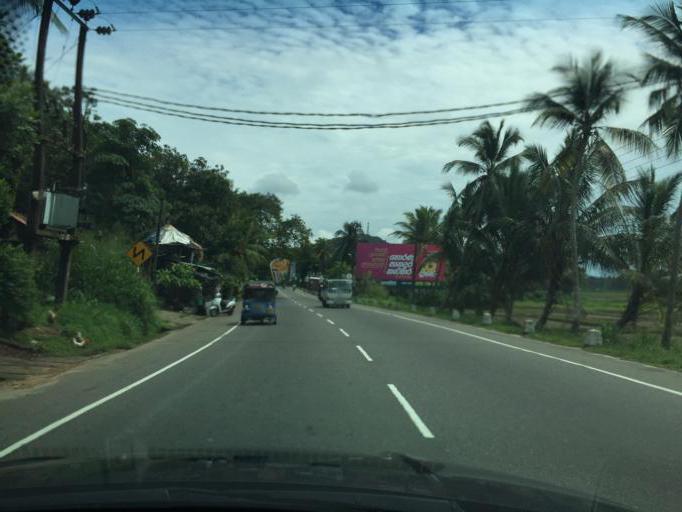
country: LK
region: Western
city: Horana South
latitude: 6.7202
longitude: 80.0500
